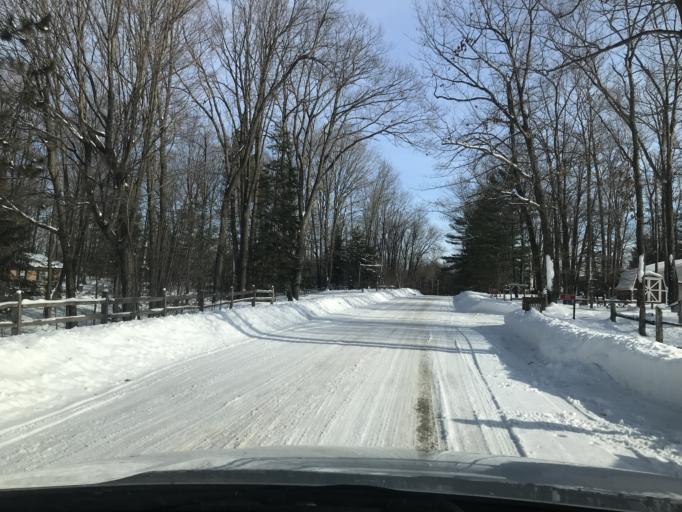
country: US
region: Wisconsin
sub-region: Oconto County
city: Gillett
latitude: 45.1537
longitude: -88.2110
